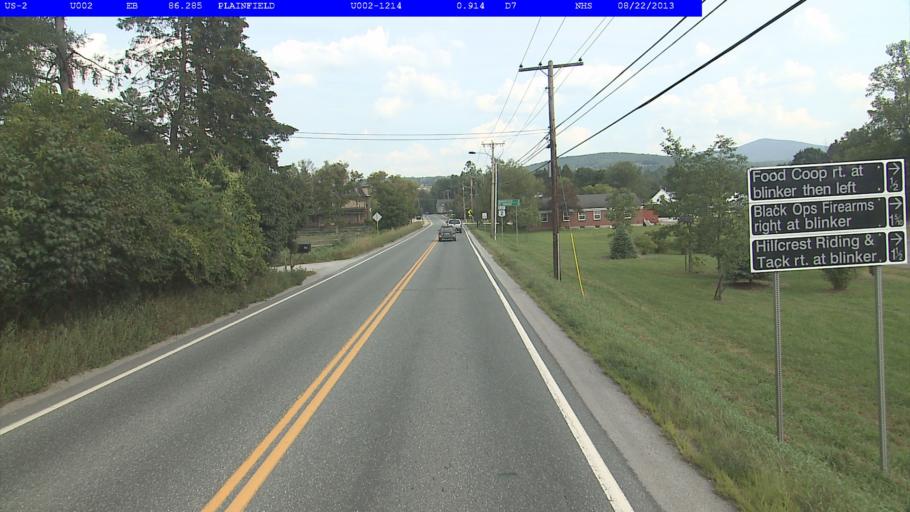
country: US
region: Vermont
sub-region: Washington County
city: Barre
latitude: 44.2782
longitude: -72.4329
